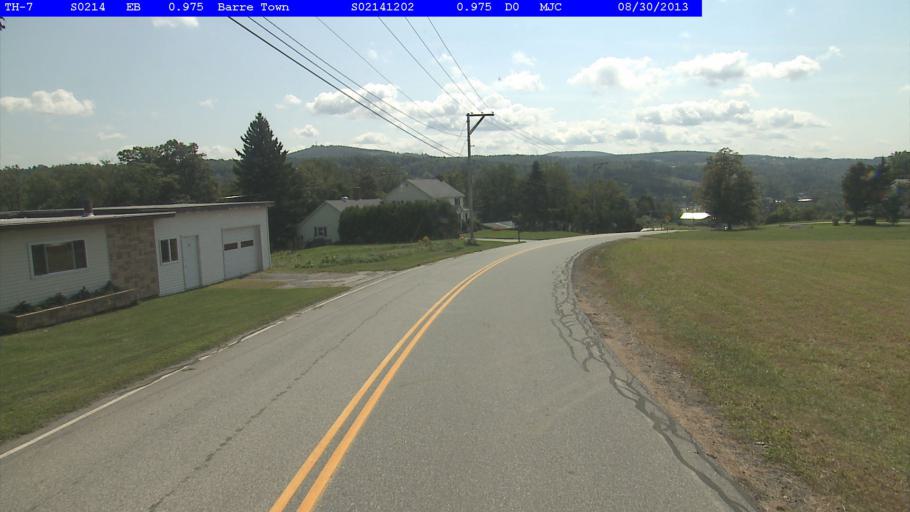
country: US
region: Vermont
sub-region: Washington County
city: South Barre
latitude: 44.1803
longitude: -72.5103
